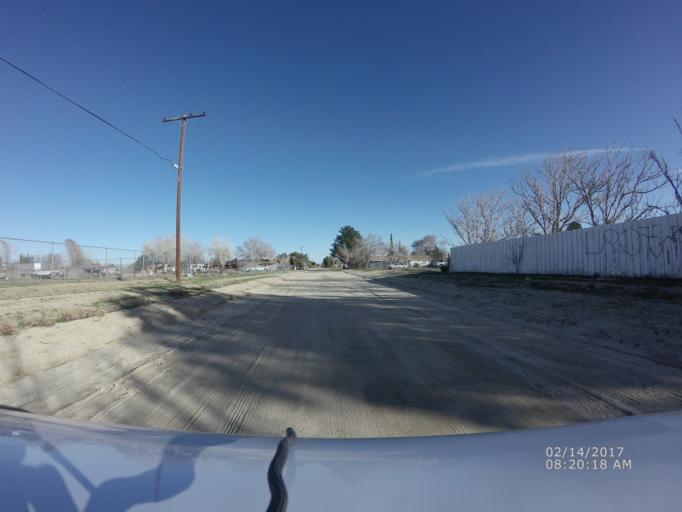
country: US
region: California
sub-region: Los Angeles County
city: Littlerock
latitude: 34.5510
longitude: -117.9538
